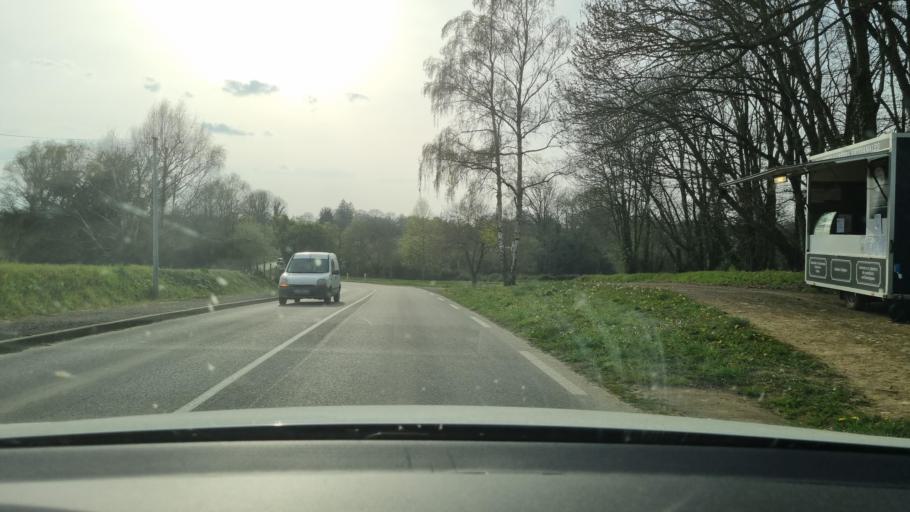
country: FR
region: Aquitaine
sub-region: Departement des Pyrenees-Atlantiques
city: Morlaas
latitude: 43.3590
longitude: -0.2271
